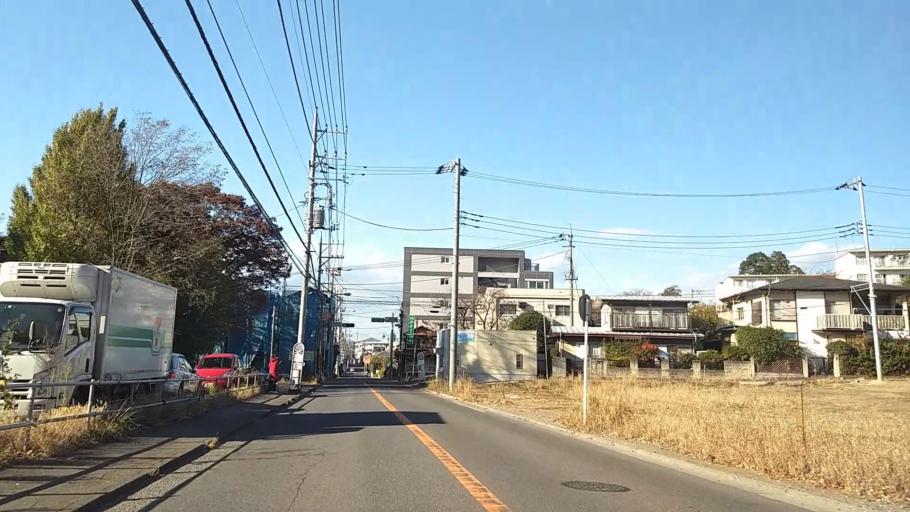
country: JP
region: Tokyo
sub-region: Machida-shi
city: Machida
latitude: 35.5227
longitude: 139.5530
